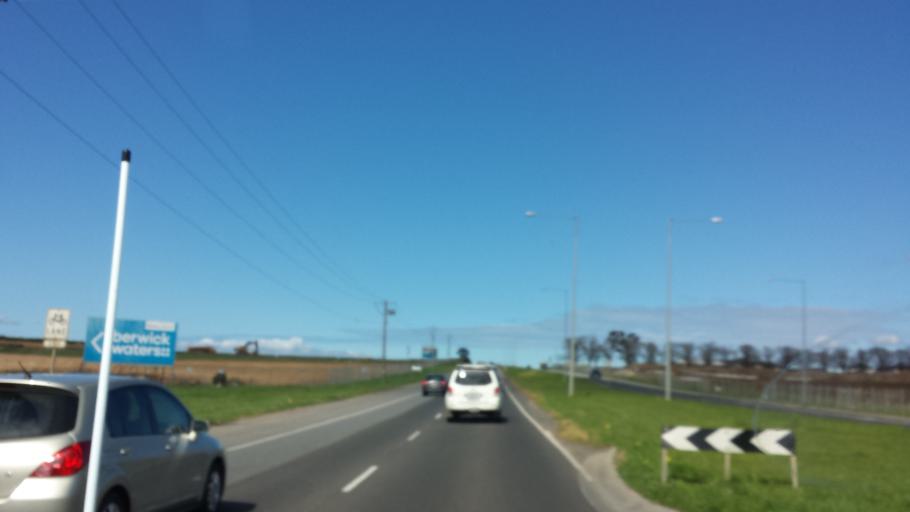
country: AU
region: Victoria
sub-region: Casey
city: Berwick
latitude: -38.0746
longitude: 145.3355
